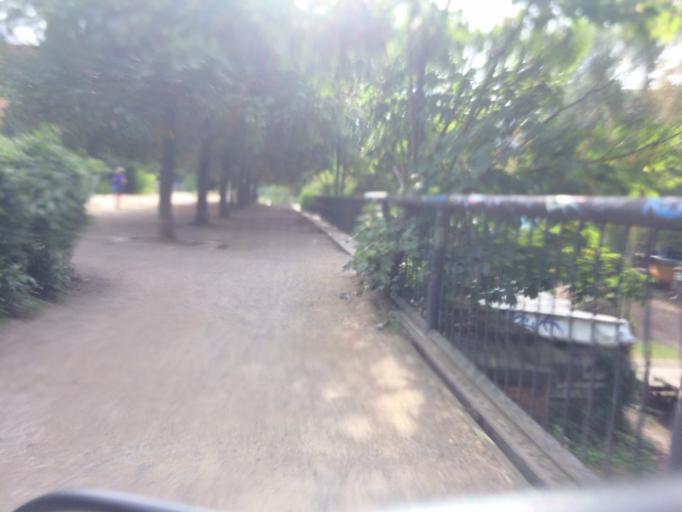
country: DE
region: Berlin
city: Berlin Treptow
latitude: 52.4942
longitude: 13.4444
